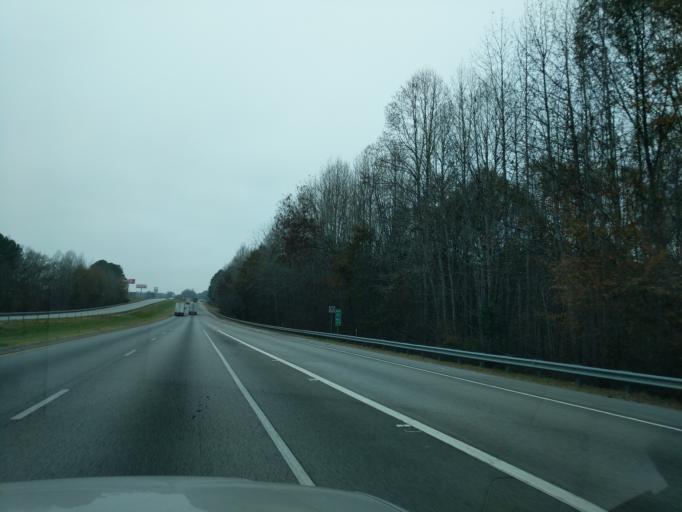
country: US
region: Georgia
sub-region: Franklin County
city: Lavonia
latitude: 34.4465
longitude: -83.1236
